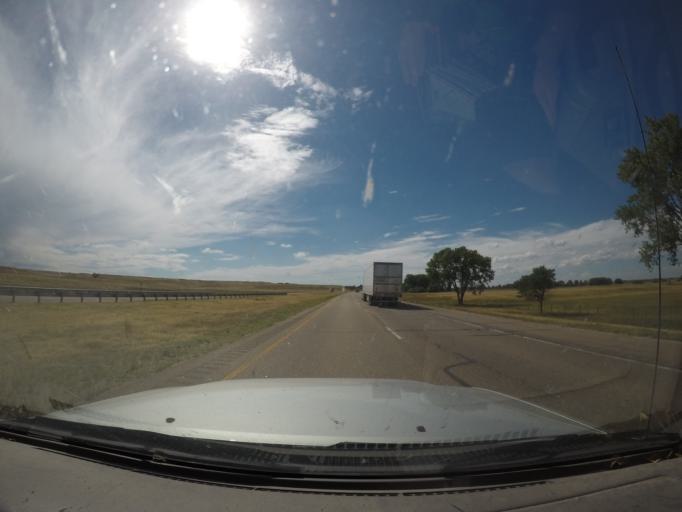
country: US
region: Nebraska
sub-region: Deuel County
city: Chappell
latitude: 41.0578
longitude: -102.4303
